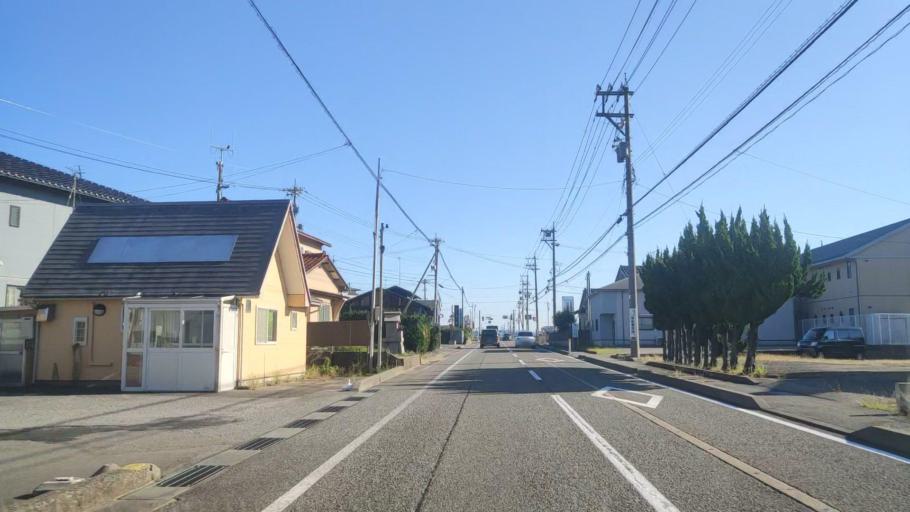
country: JP
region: Ishikawa
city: Tsubata
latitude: 36.7744
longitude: 136.7302
